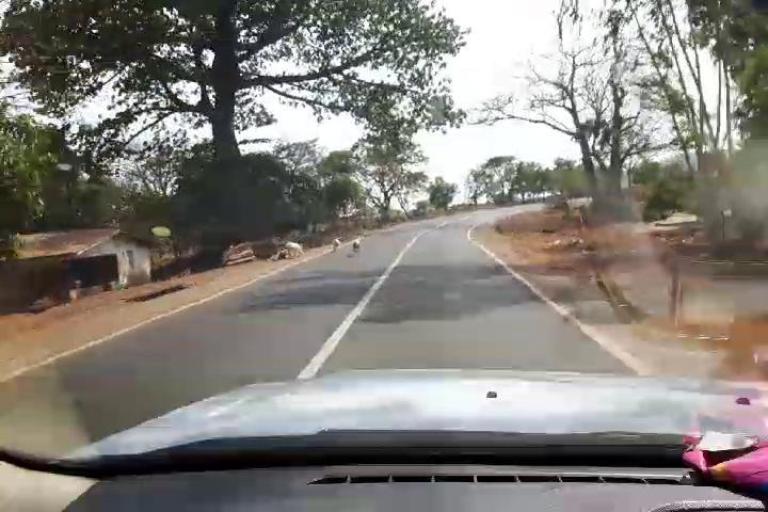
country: SL
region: Western Area
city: Waterloo
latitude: 8.2024
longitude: -13.1179
